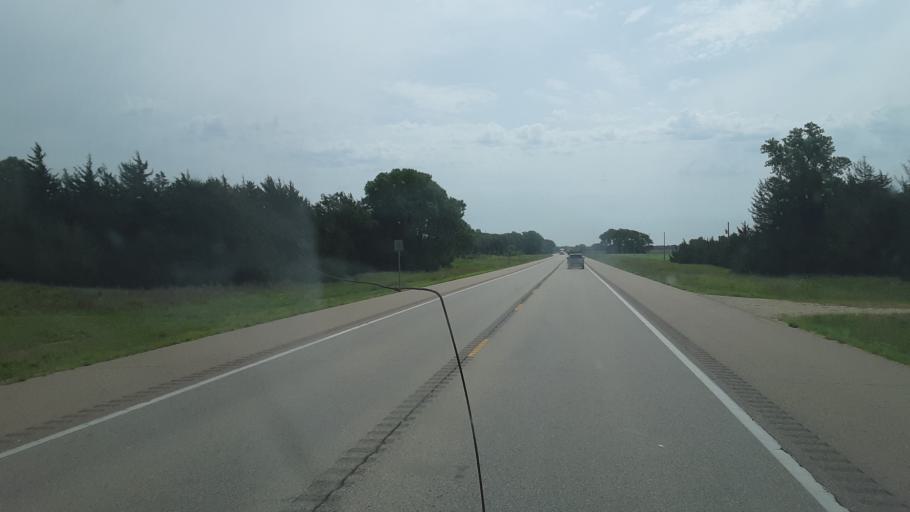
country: US
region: Kansas
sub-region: Rice County
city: Sterling
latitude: 37.9846
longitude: -98.2583
